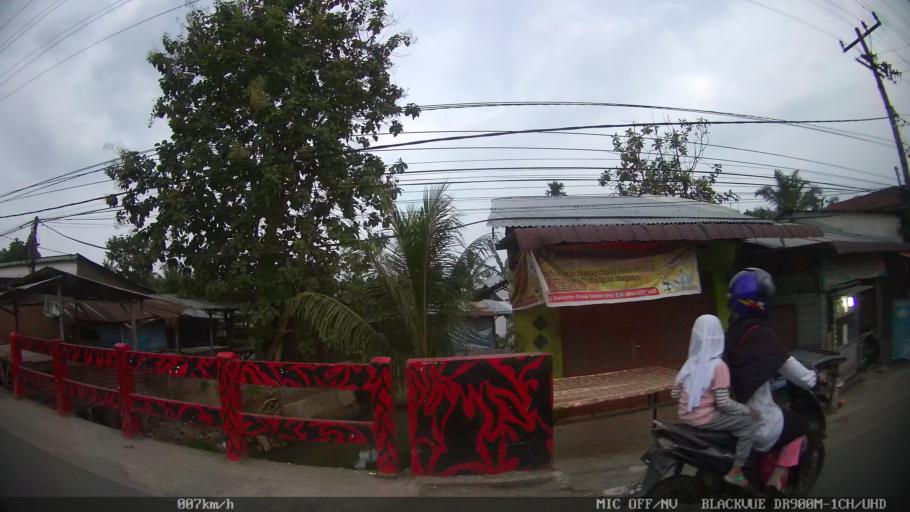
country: ID
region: North Sumatra
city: Sunggal
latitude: 3.5765
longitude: 98.5879
